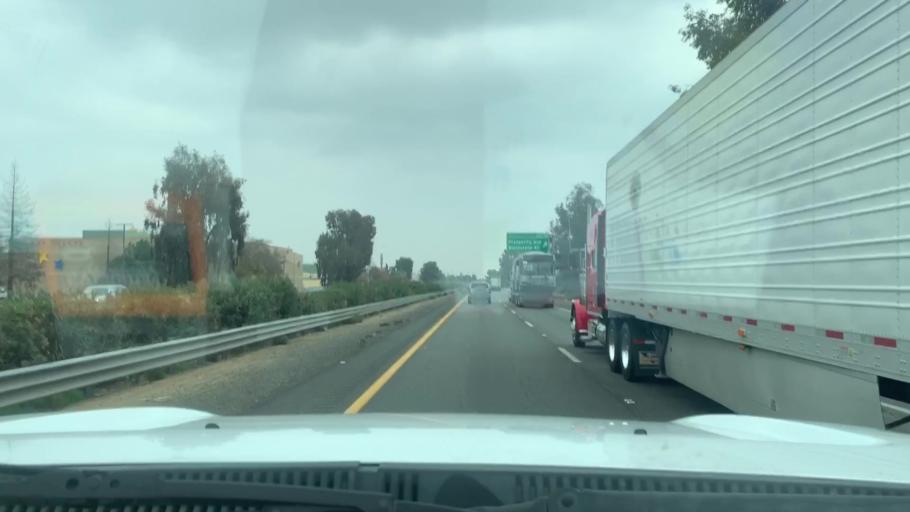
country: US
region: California
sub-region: Tulare County
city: Tulare
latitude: 36.2292
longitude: -119.3377
